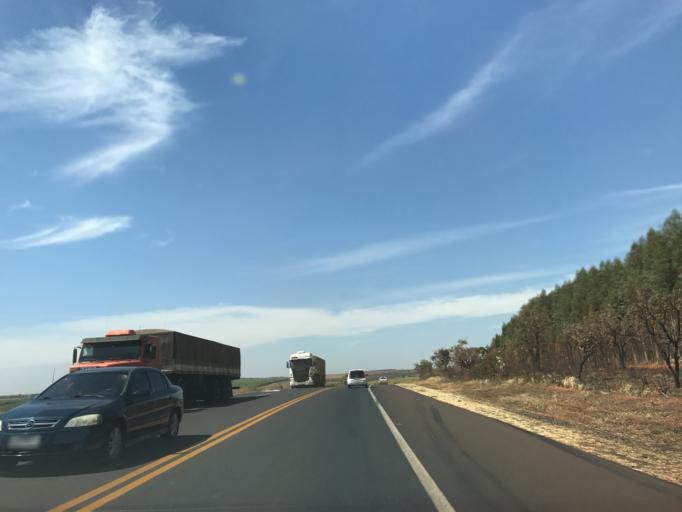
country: BR
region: Minas Gerais
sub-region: Prata
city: Prata
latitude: -19.1135
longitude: -48.9716
